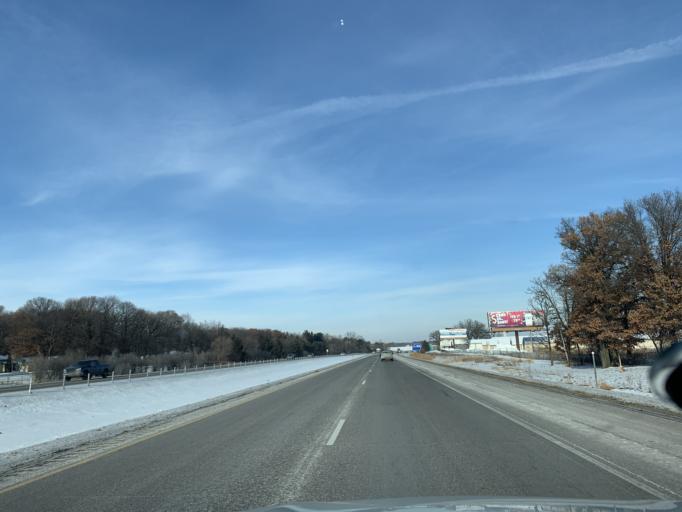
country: US
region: Minnesota
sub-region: Chisago County
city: Wyoming
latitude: 45.3277
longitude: -93.0039
